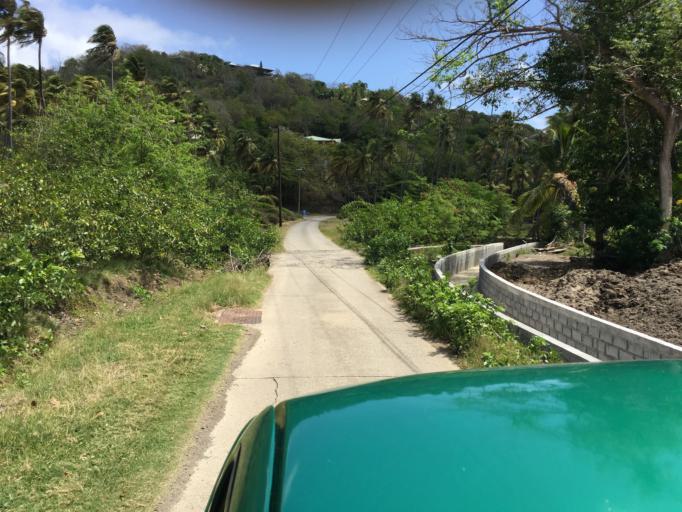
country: VC
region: Grenadines
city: Port Elizabeth
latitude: 13.0211
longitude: -61.2237
